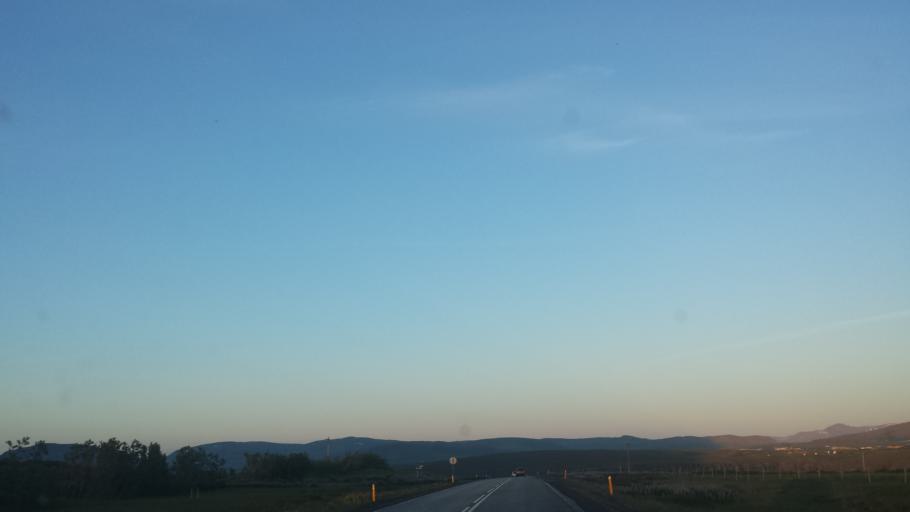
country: IS
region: Capital Region
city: Mosfellsbaer
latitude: 64.2087
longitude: -21.7634
